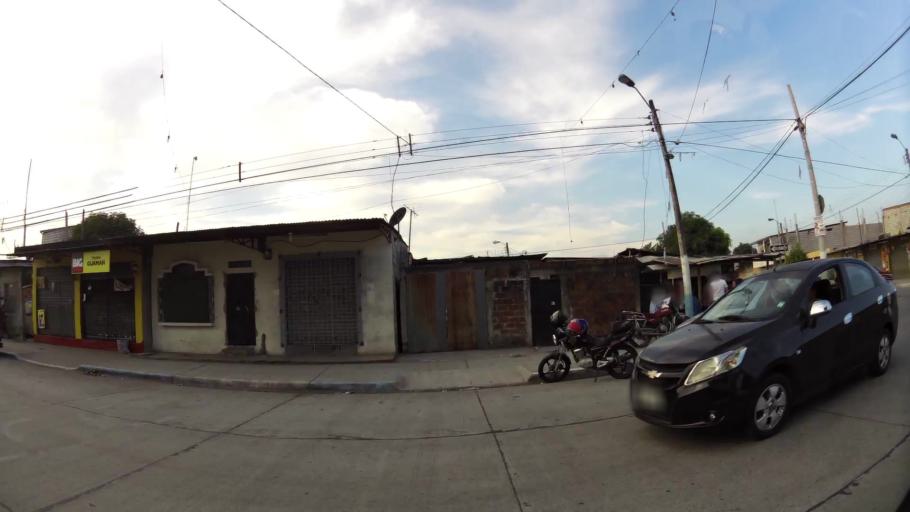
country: EC
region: Guayas
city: Eloy Alfaro
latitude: -2.0894
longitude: -79.8973
